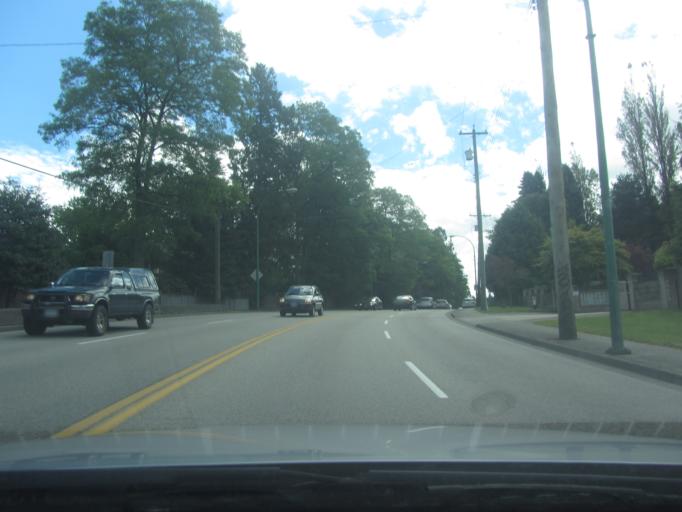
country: CA
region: British Columbia
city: Burnaby
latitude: 49.2379
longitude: -122.9575
